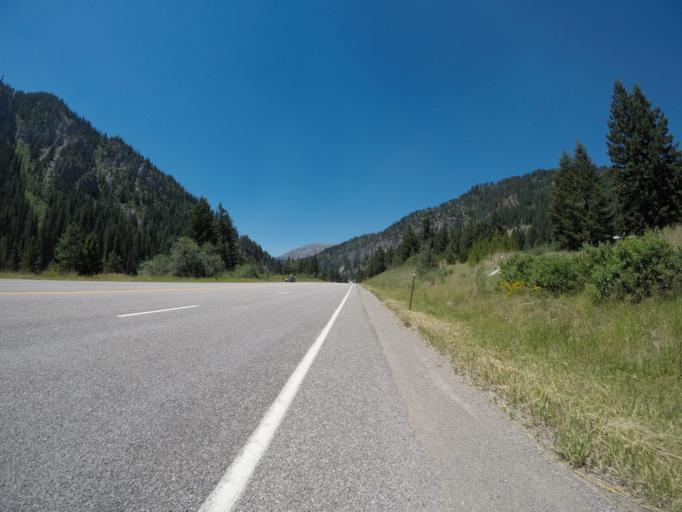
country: US
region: Wyoming
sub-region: Teton County
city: Hoback
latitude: 43.1976
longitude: -110.8945
